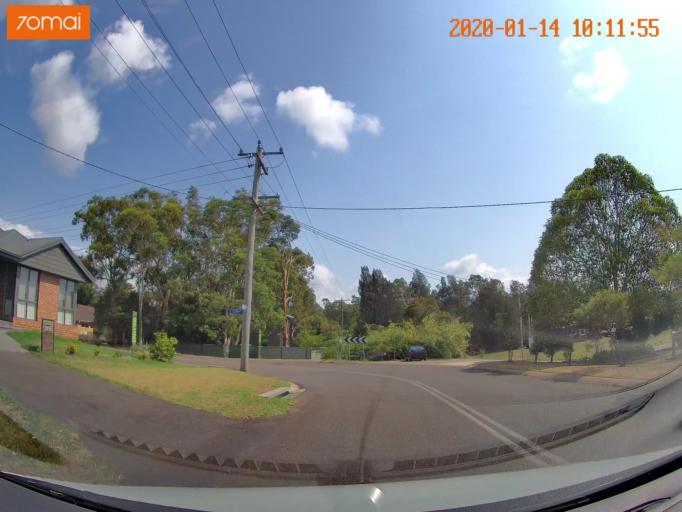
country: AU
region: New South Wales
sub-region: Lake Macquarie Shire
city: Dora Creek
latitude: -33.1184
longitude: 151.5315
